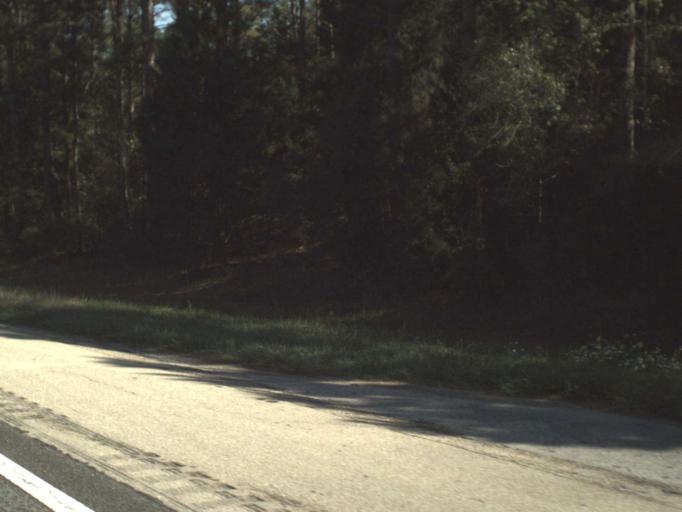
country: US
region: Florida
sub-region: Washington County
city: Chipley
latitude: 30.7451
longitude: -85.4618
